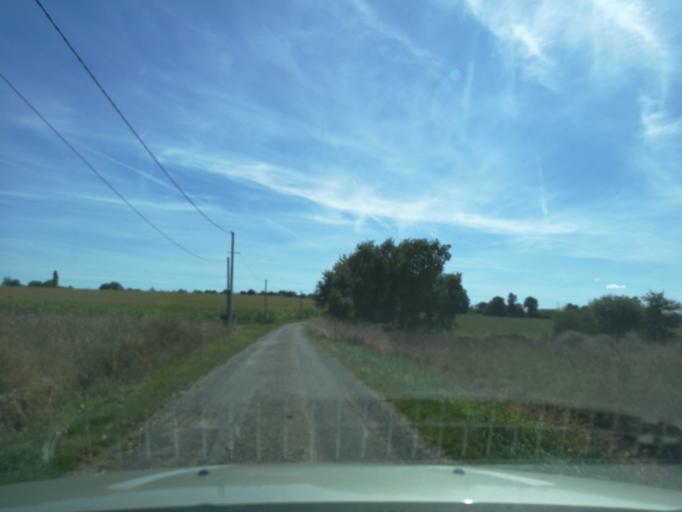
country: FR
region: Brittany
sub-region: Departement d'Ille-et-Vilaine
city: Bedee
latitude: 48.1605
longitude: -1.9552
